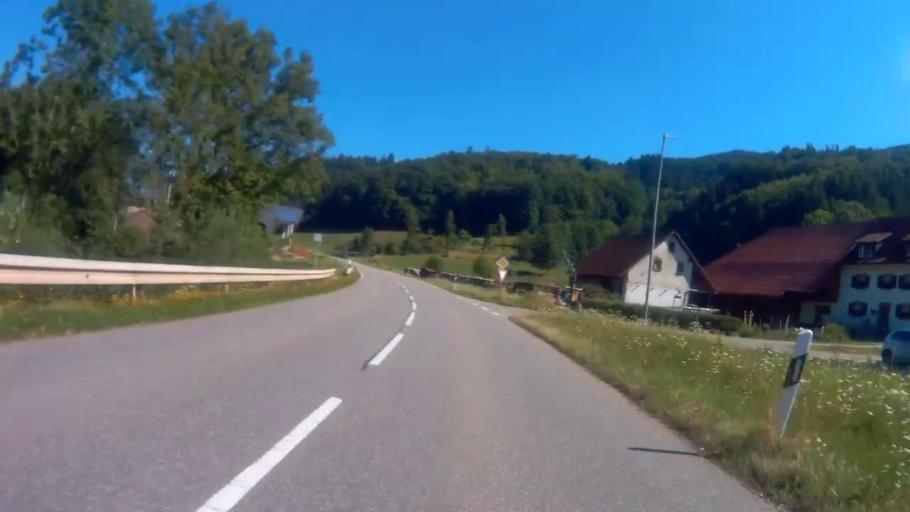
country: DE
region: Baden-Wuerttemberg
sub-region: Freiburg Region
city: Hausen
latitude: 47.7044
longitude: 7.7995
